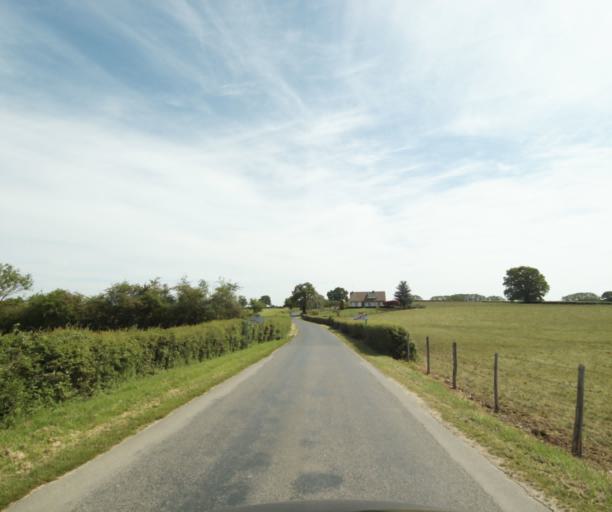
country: FR
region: Bourgogne
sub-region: Departement de Saone-et-Loire
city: Paray-le-Monial
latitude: 46.5367
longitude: 4.1324
